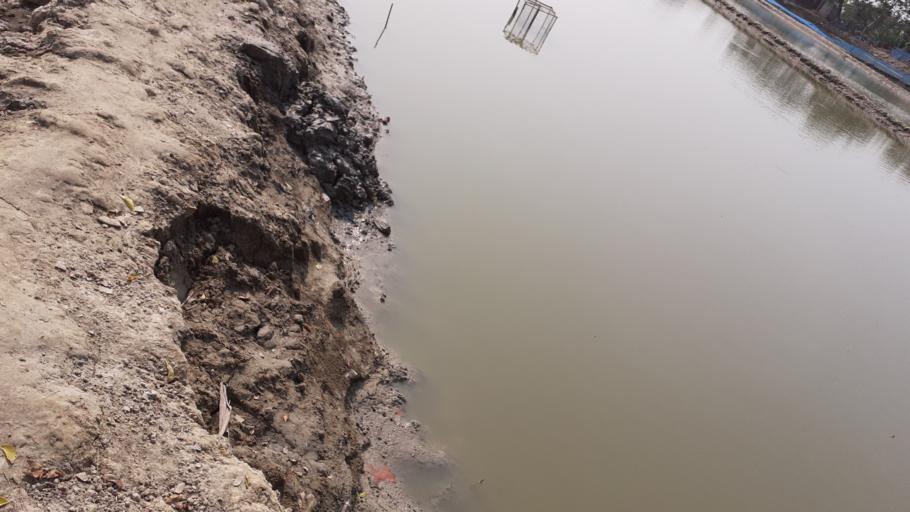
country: BD
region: Khulna
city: Phultala
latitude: 22.6544
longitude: 89.3979
